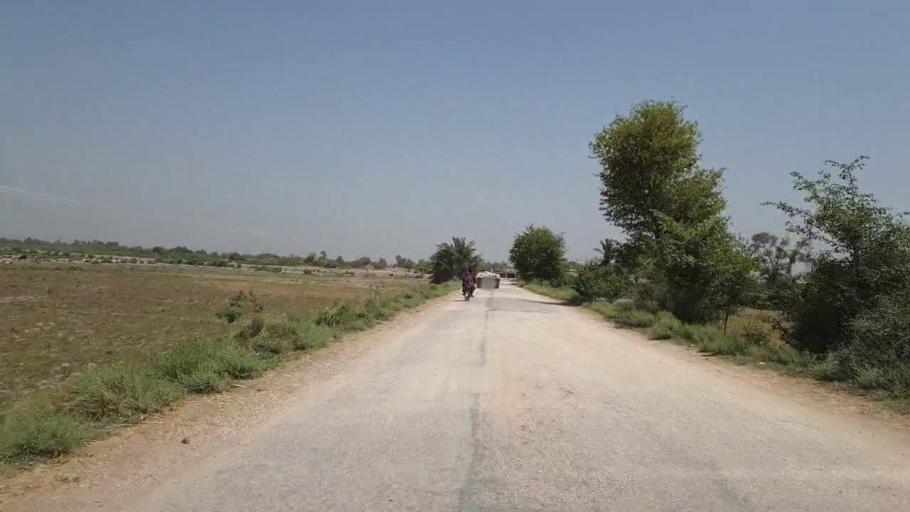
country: PK
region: Sindh
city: Adilpur
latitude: 27.8893
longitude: 69.2887
